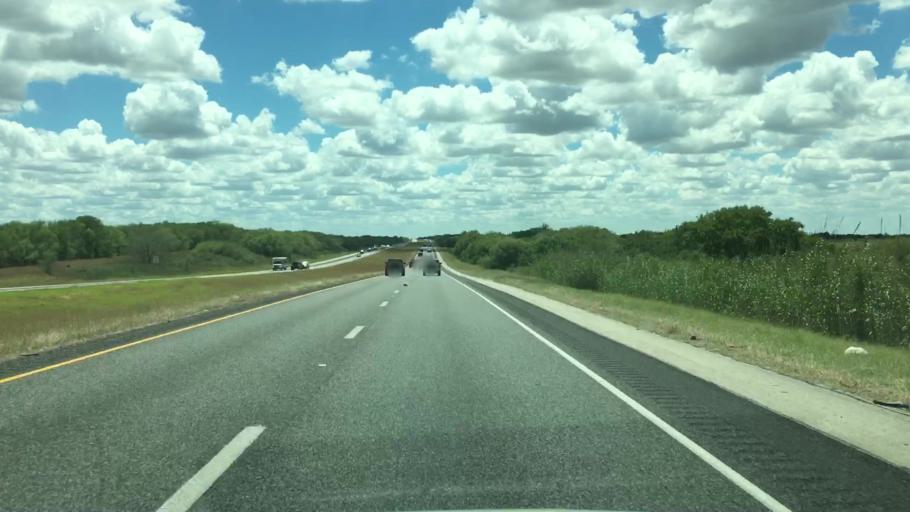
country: US
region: Texas
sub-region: Atascosa County
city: Pleasanton
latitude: 29.0855
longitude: -98.4331
